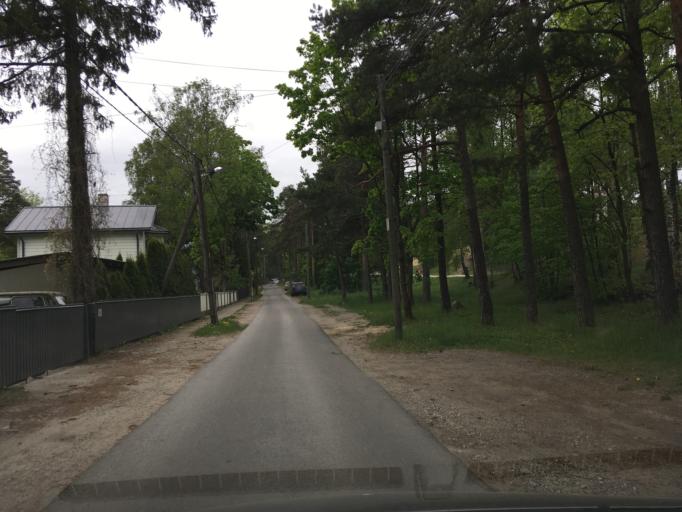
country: EE
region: Harju
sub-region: Saue vald
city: Laagri
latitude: 59.3878
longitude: 24.6717
